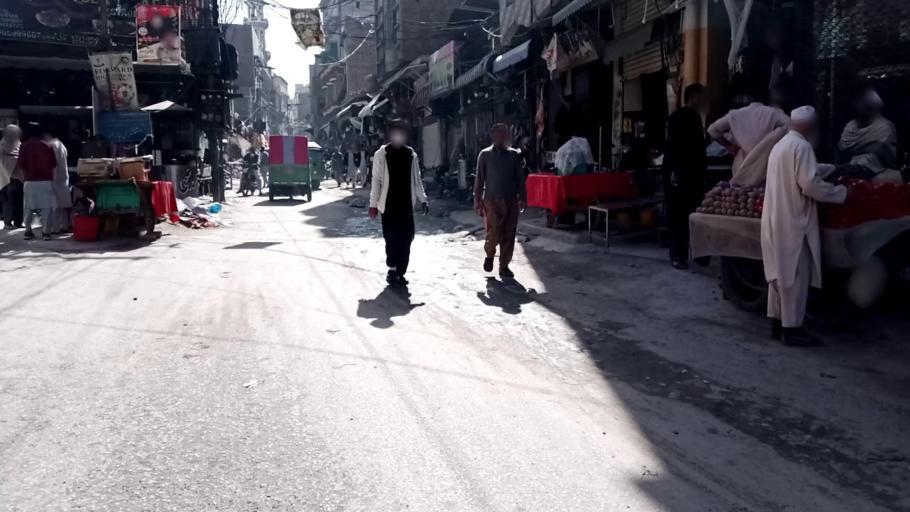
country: PK
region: Khyber Pakhtunkhwa
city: Peshawar
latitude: 34.0132
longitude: 71.5806
